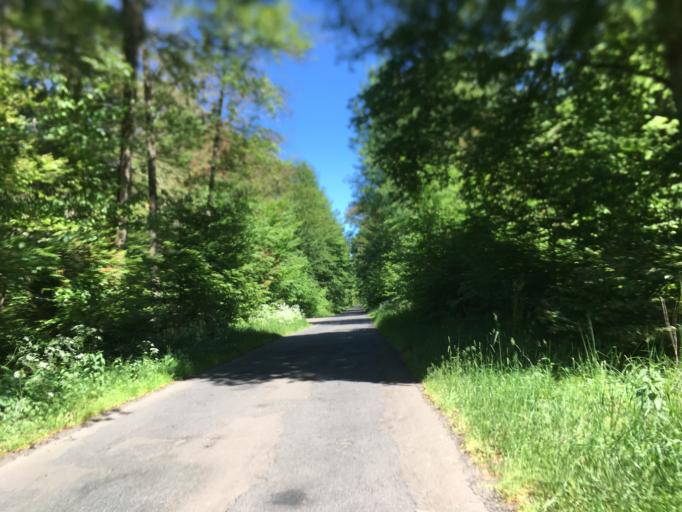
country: DE
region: Brandenburg
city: Zehdenick
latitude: 53.0011
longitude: 13.4336
